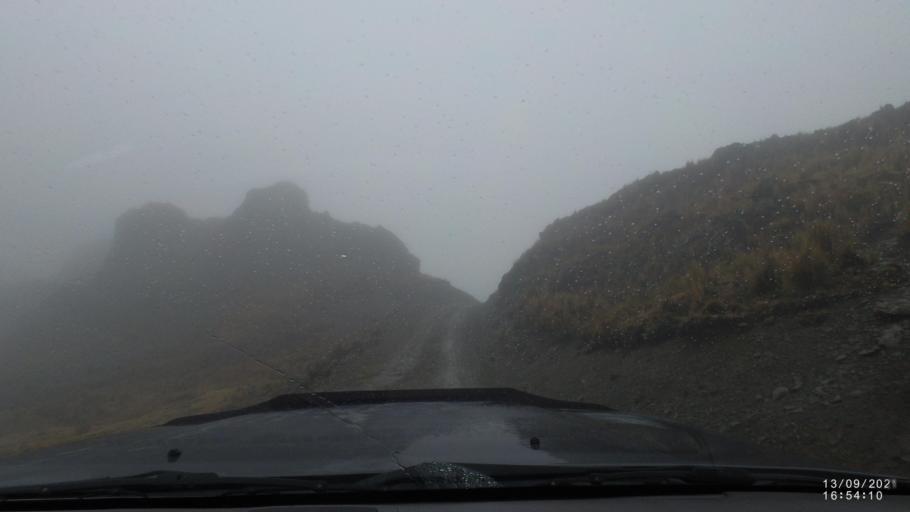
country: BO
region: Cochabamba
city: Colomi
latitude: -17.3037
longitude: -65.7119
